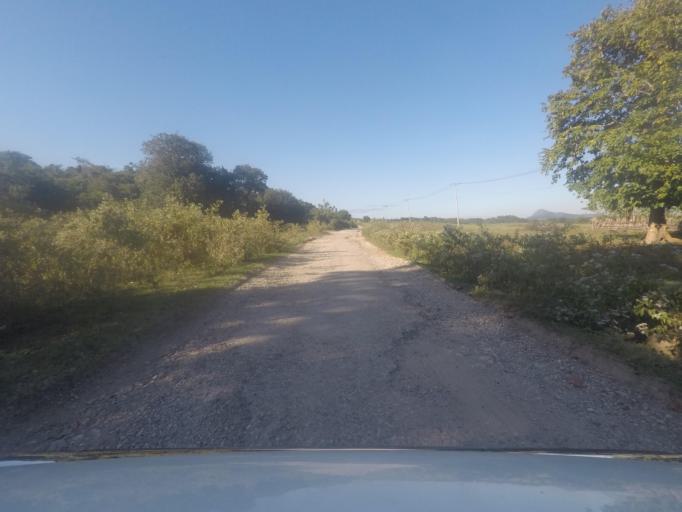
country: TL
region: Lautem
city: Lospalos
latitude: -8.4071
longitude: 127.1724
